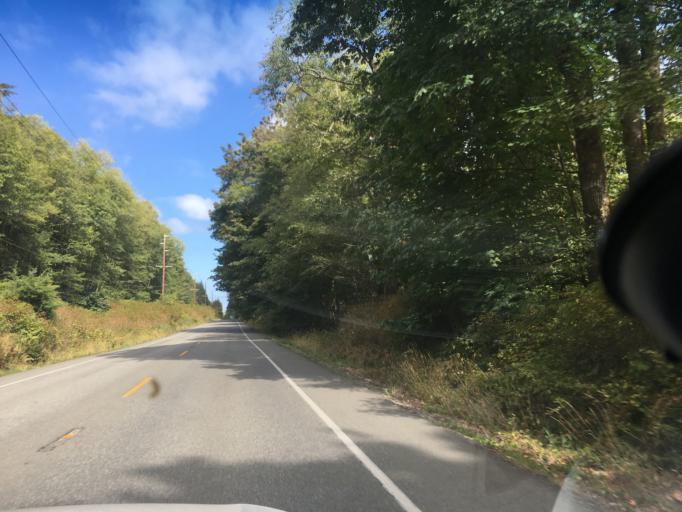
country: US
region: Washington
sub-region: Kitsap County
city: Lofall
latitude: 47.8327
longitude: -122.5865
